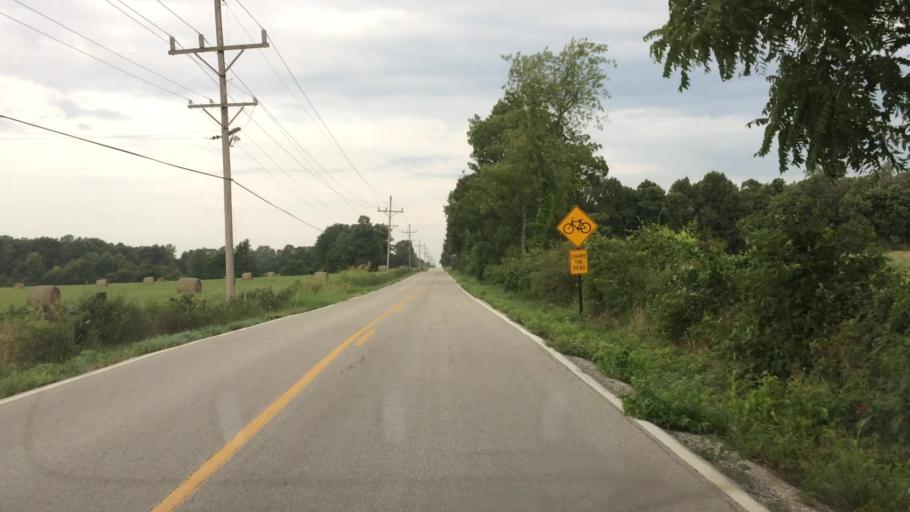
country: US
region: Missouri
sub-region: Greene County
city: Strafford
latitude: 37.2710
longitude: -93.1384
